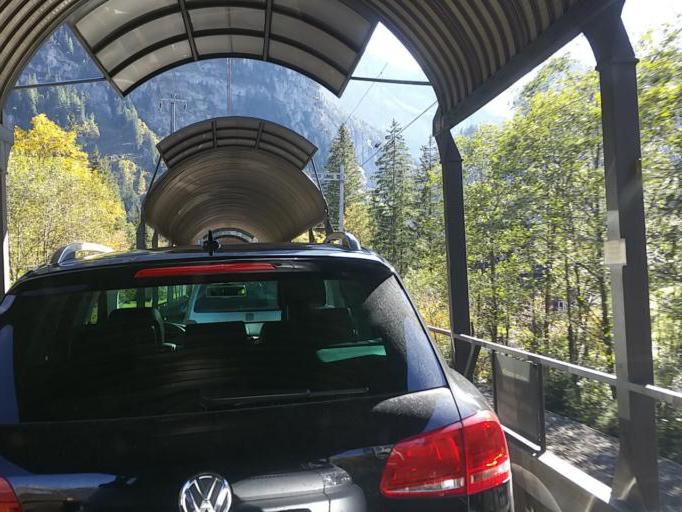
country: CH
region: Bern
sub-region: Frutigen-Niedersimmental District
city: Kandersteg
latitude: 46.4831
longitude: 7.6656
